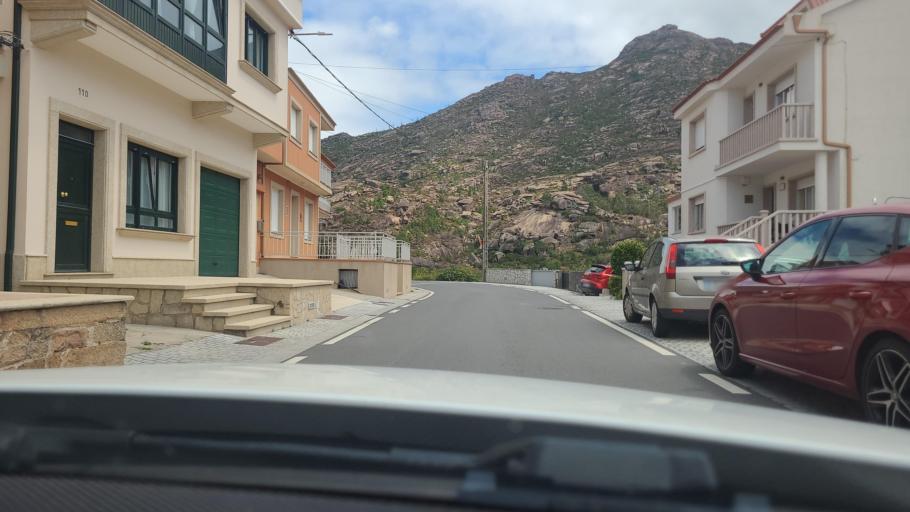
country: ES
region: Galicia
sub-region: Provincia da Coruna
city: Corcubion
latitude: 42.9079
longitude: -9.1261
